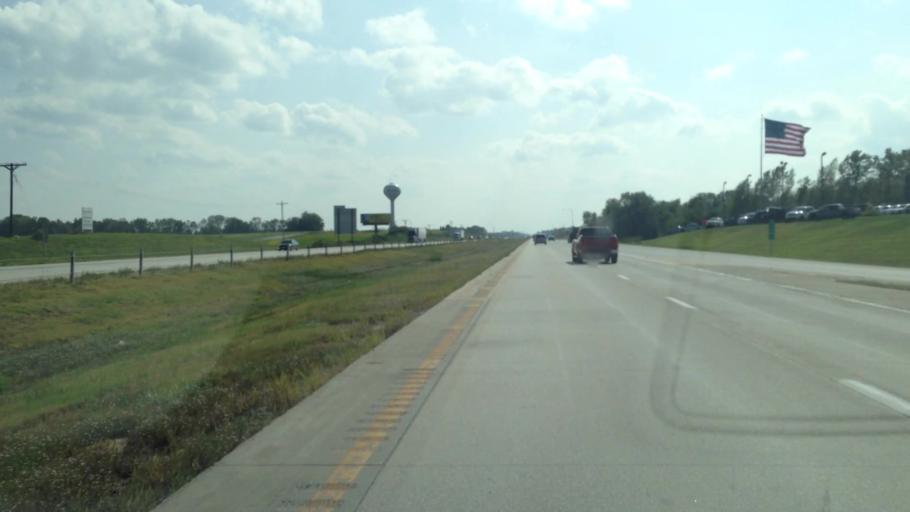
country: US
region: Missouri
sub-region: Clay County
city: Kearney
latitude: 39.3664
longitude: -94.3733
